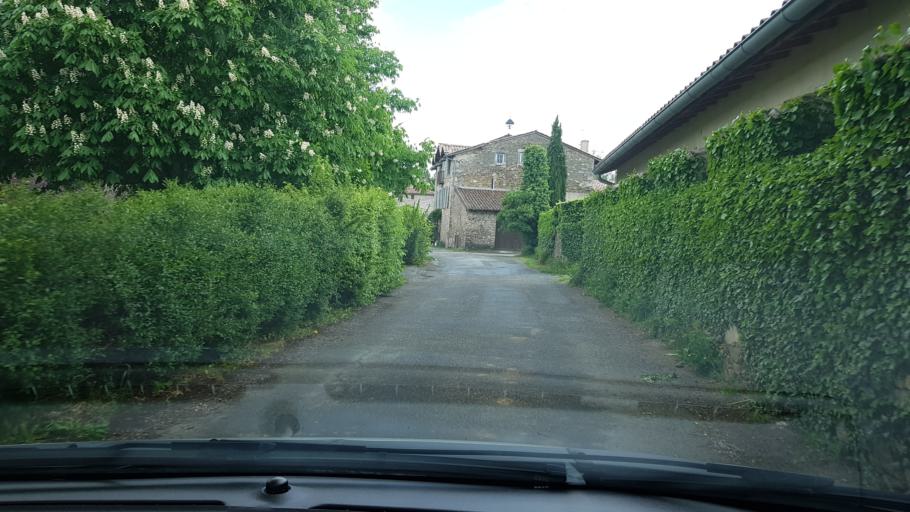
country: FR
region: Rhone-Alpes
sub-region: Departement du Rhone
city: Saint-Maurice-sur-Dargoire
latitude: 45.5782
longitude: 4.6437
